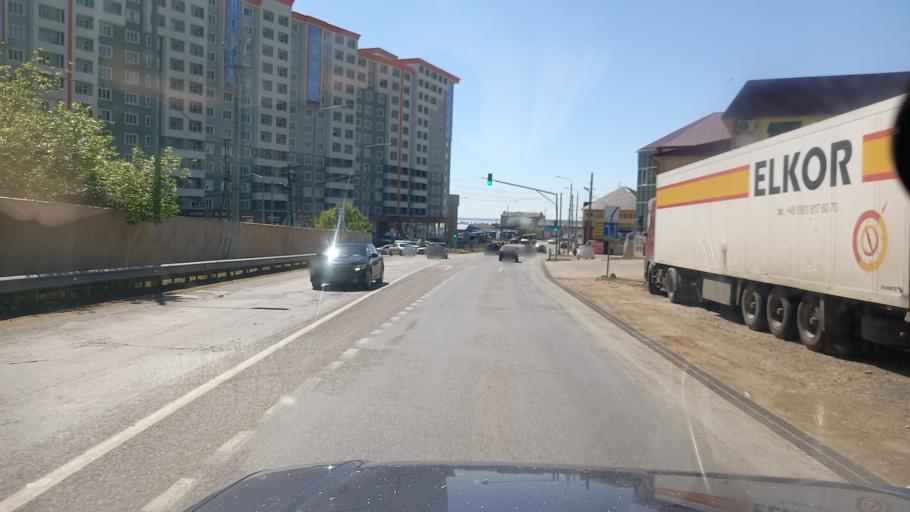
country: RU
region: Dagestan
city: Derbent
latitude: 42.0363
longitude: 48.2934
